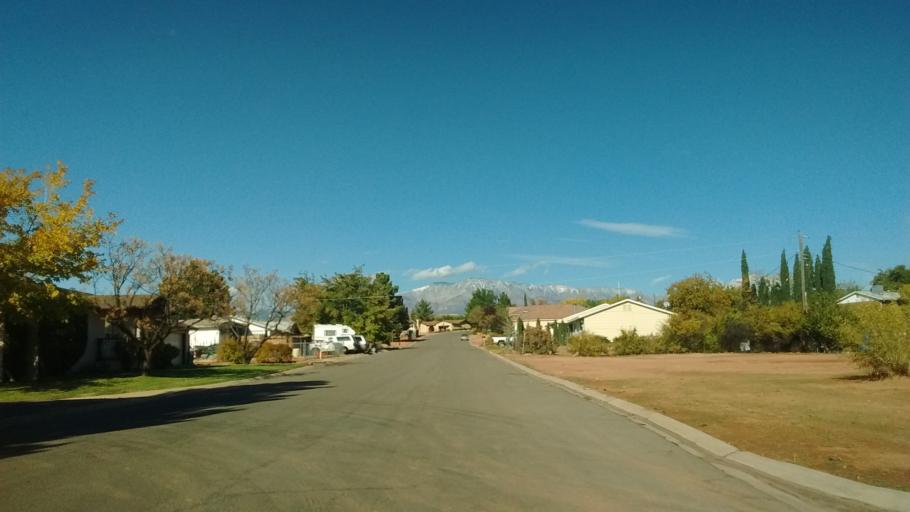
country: US
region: Utah
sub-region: Washington County
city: Washington
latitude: 37.1319
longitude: -113.4975
